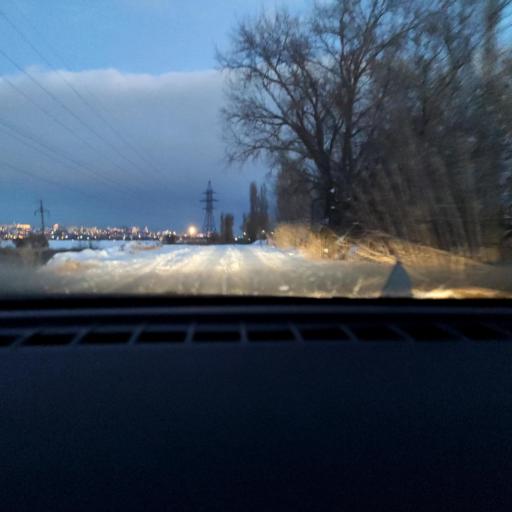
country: RU
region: Voronezj
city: Voronezh
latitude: 51.6213
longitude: 39.2200
